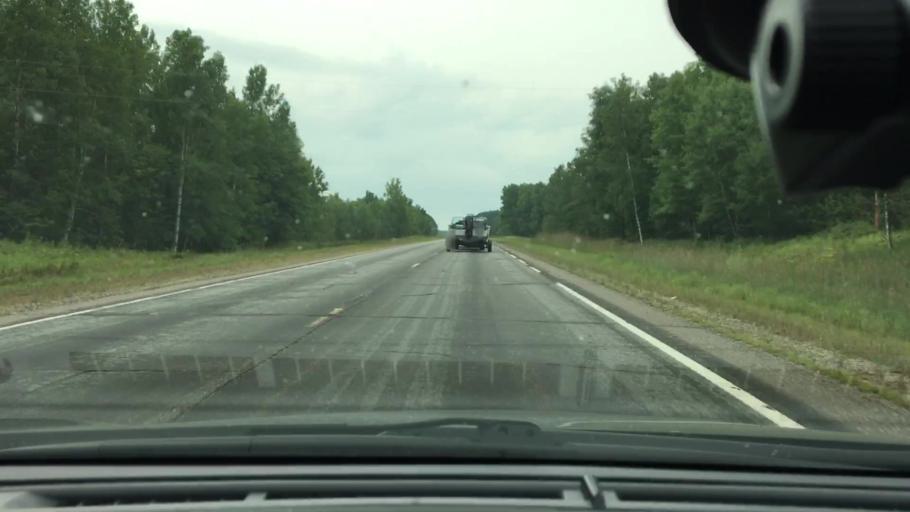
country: US
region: Minnesota
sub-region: Crow Wing County
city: Crosby
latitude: 46.6424
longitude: -93.9512
